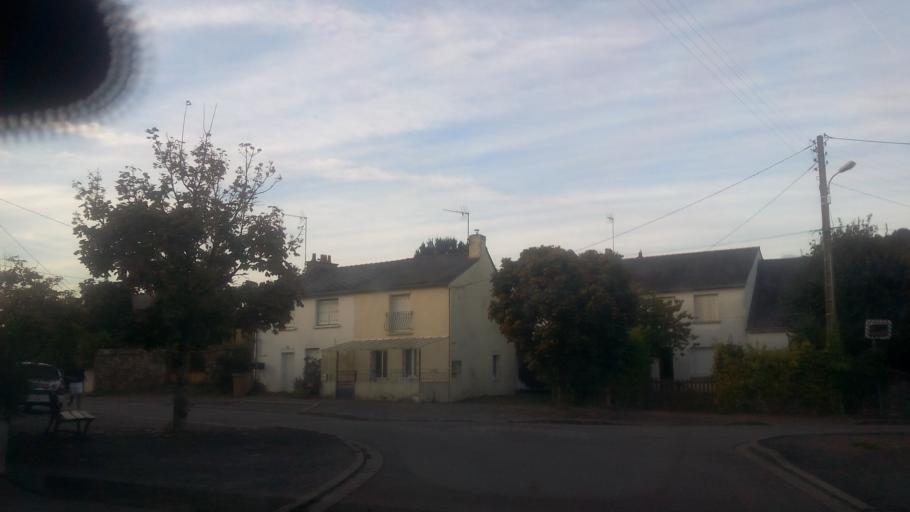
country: FR
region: Brittany
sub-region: Departement d'Ille-et-Vilaine
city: Redon
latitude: 47.6611
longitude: -2.0905
